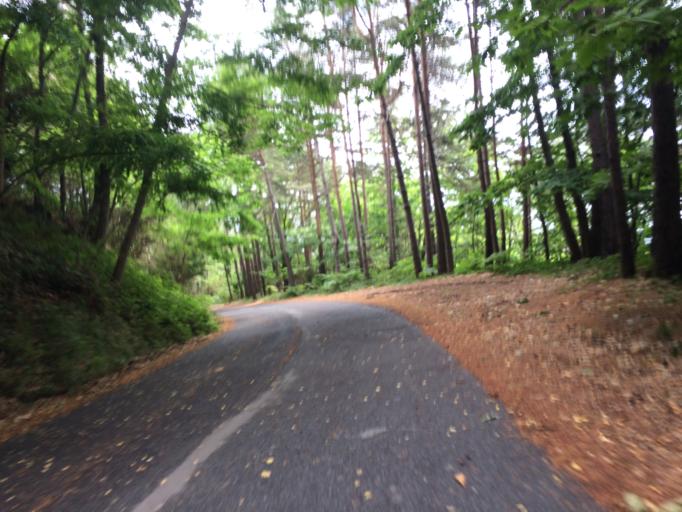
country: IT
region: Liguria
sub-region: Provincia di Imperia
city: Bajardo
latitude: 43.8888
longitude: 7.7337
